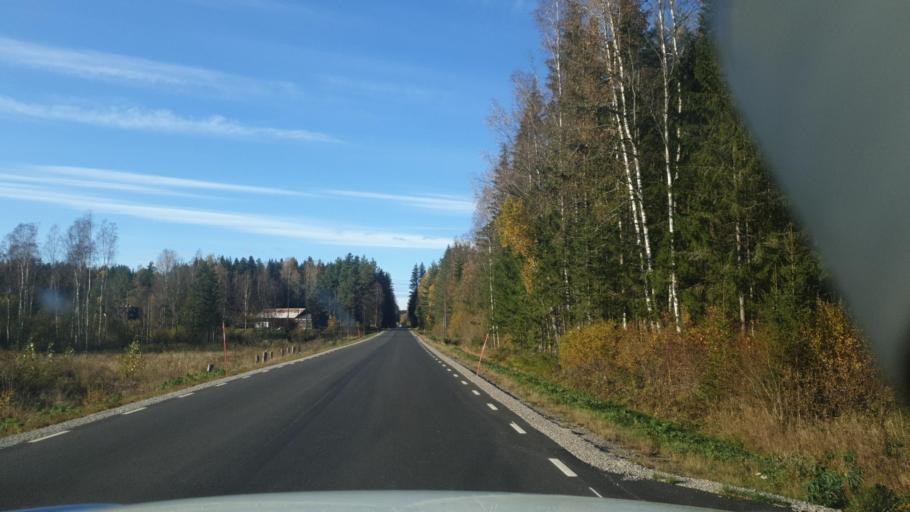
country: SE
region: Vaermland
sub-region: Arvika Kommun
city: Arvika
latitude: 59.6522
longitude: 12.7348
